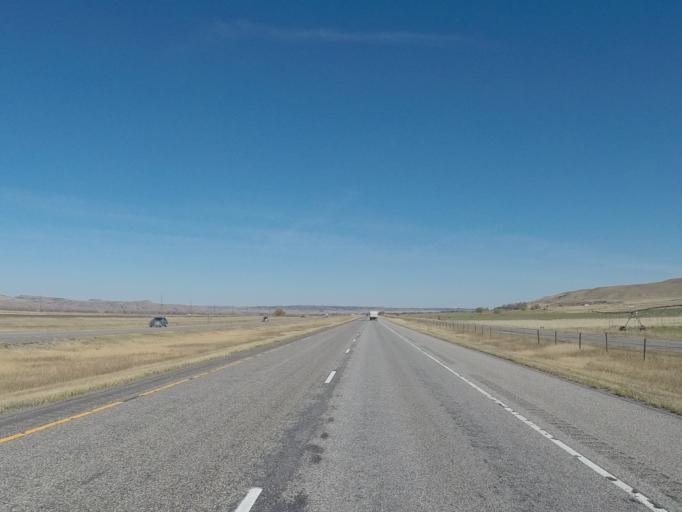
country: US
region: Montana
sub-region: Sweet Grass County
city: Big Timber
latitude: 45.8086
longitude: -110.0131
